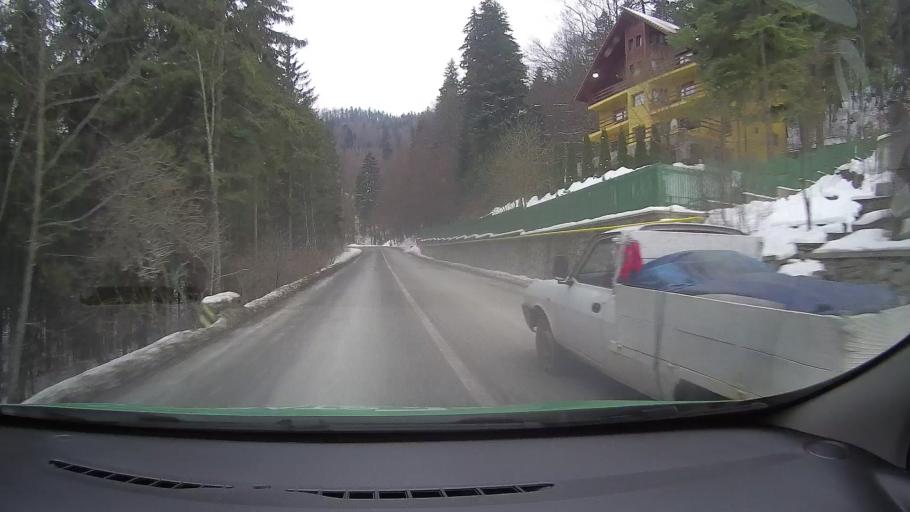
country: RO
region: Brasov
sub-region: Oras Predeal
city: Predeal
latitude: 45.5165
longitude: 25.5032
